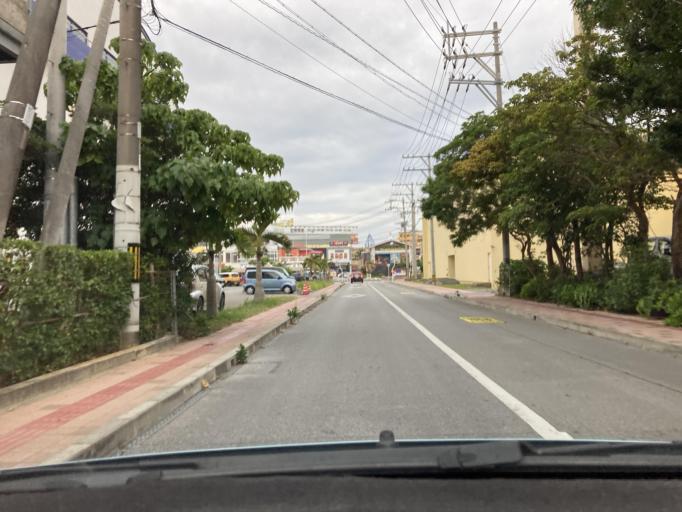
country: JP
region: Okinawa
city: Chatan
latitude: 26.3146
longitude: 127.7565
